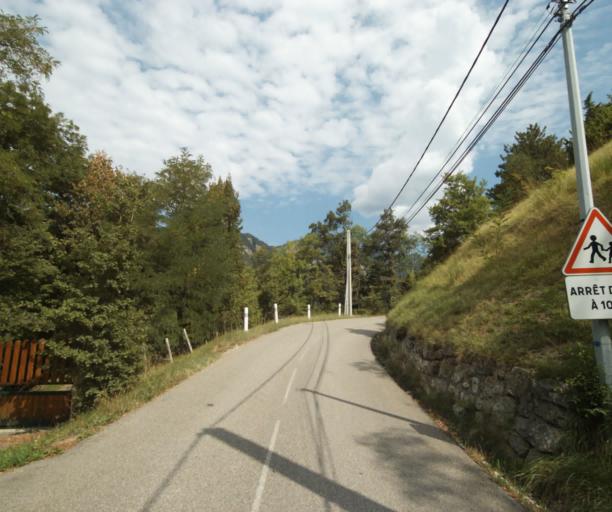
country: FR
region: Rhone-Alpes
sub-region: Departement de l'Isere
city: Le Sappey-en-Chartreuse
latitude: 45.2498
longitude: 5.7342
